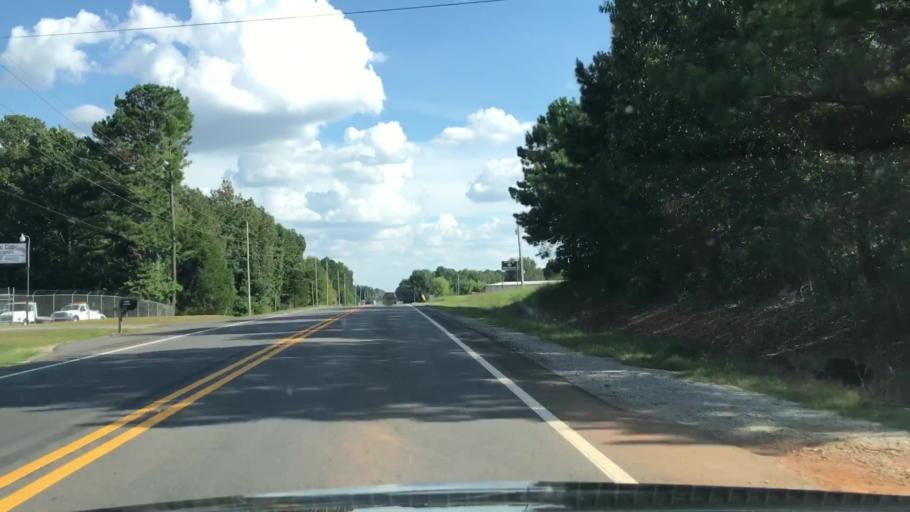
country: US
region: Alabama
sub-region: Madison County
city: Harvest
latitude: 34.9138
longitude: -86.7600
